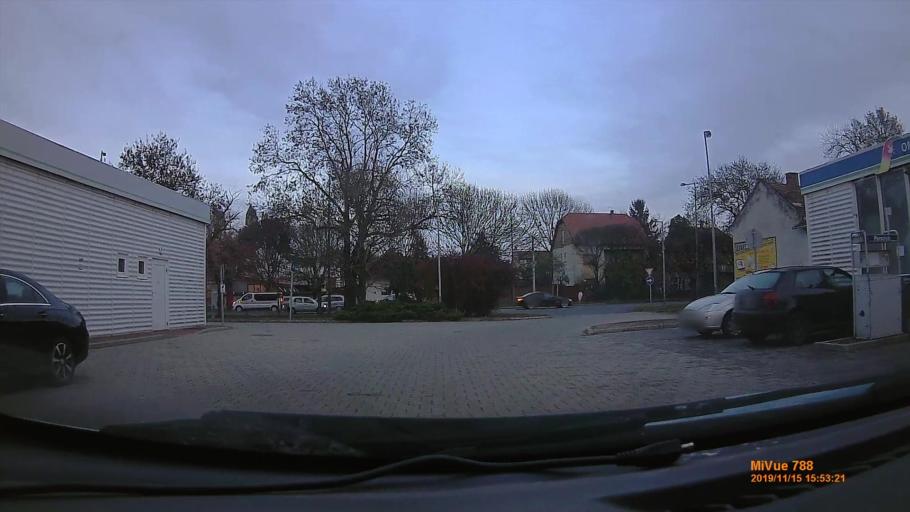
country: HU
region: Bekes
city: Bekescsaba
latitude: 46.6835
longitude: 21.0867
